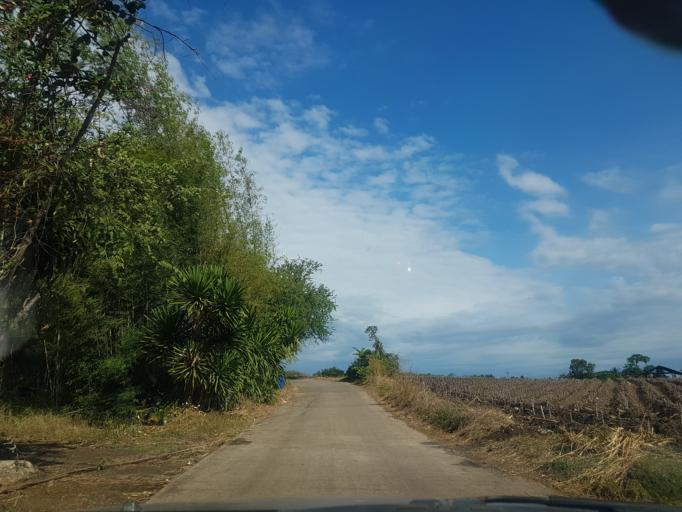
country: TH
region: Sara Buri
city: Phra Phutthabat
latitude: 14.8279
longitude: 100.7635
